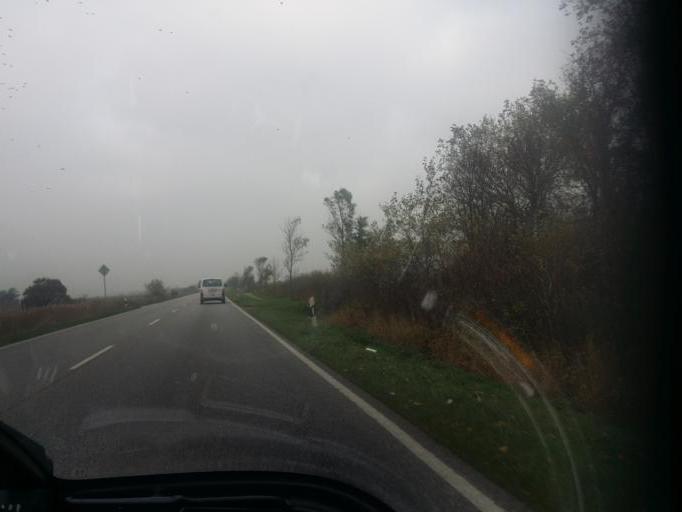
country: DE
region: Schleswig-Holstein
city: Hattstedt
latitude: 54.5347
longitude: 9.0185
